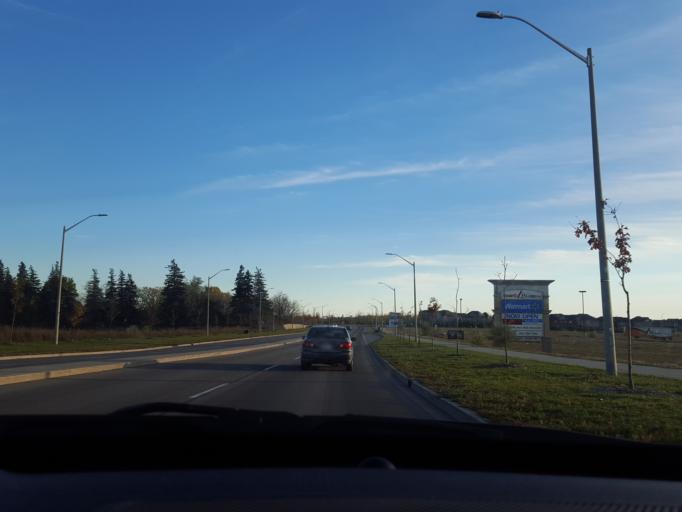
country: CA
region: Ontario
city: Markham
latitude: 43.8724
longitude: -79.2124
